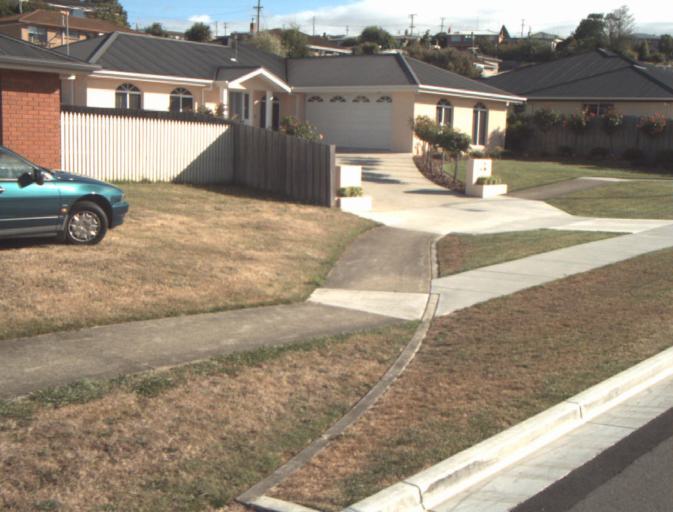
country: AU
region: Tasmania
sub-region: Launceston
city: Newnham
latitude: -41.3944
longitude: 147.1333
